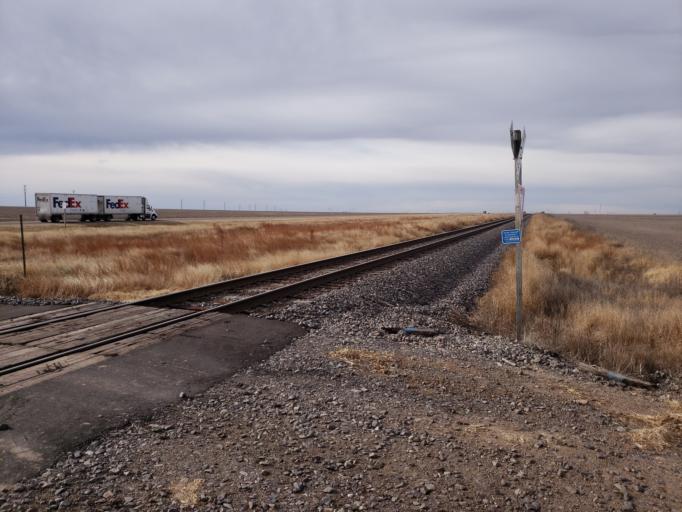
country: US
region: Kansas
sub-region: Ford County
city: Dodge City
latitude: 37.5118
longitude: -99.8132
